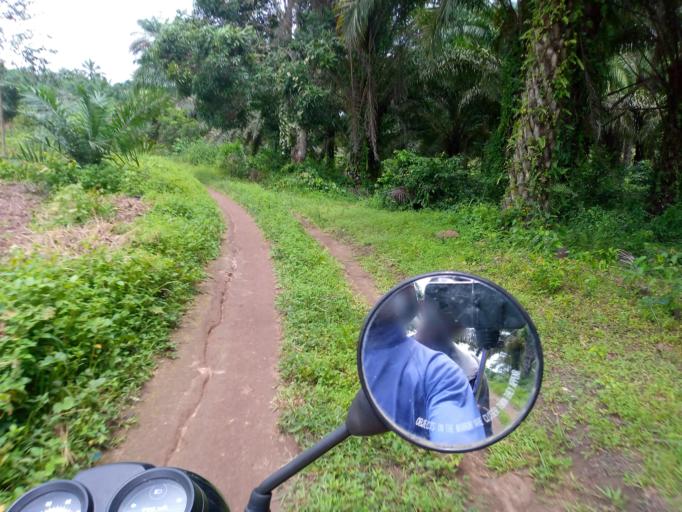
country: SL
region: Northern Province
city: Mange
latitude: 8.9874
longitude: -12.7220
